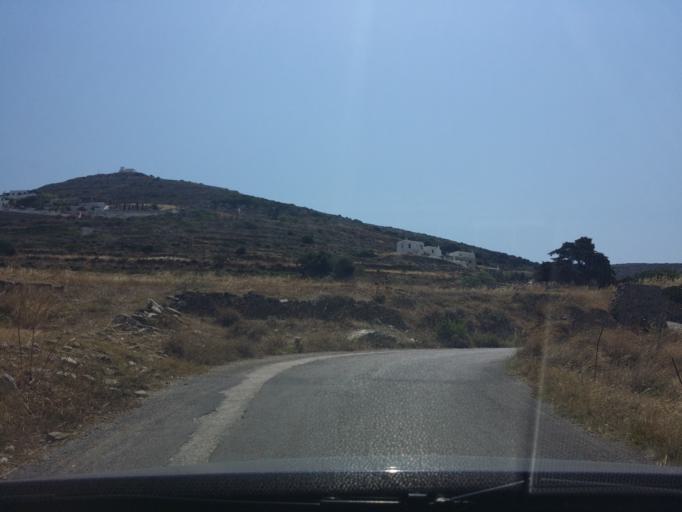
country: GR
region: South Aegean
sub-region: Nomos Kykladon
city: Paros
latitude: 37.0472
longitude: 25.1251
